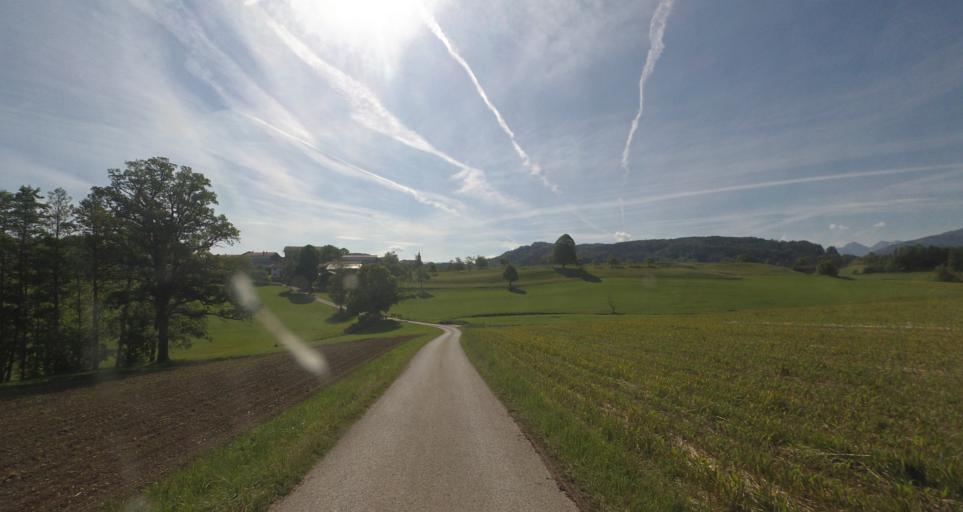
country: DE
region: Bavaria
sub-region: Upper Bavaria
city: Vachendorf
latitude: 47.8445
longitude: 12.5955
